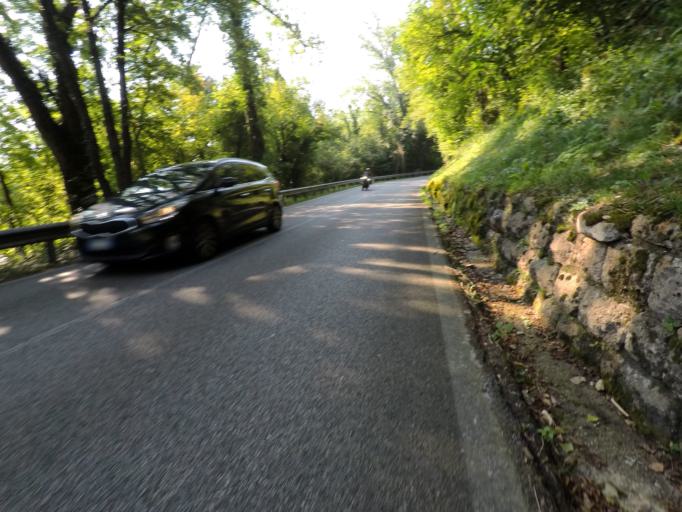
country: IT
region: Friuli Venezia Giulia
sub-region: Provincia di Pordenone
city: Pinzano al Tagliamento
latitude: 46.1898
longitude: 12.9507
